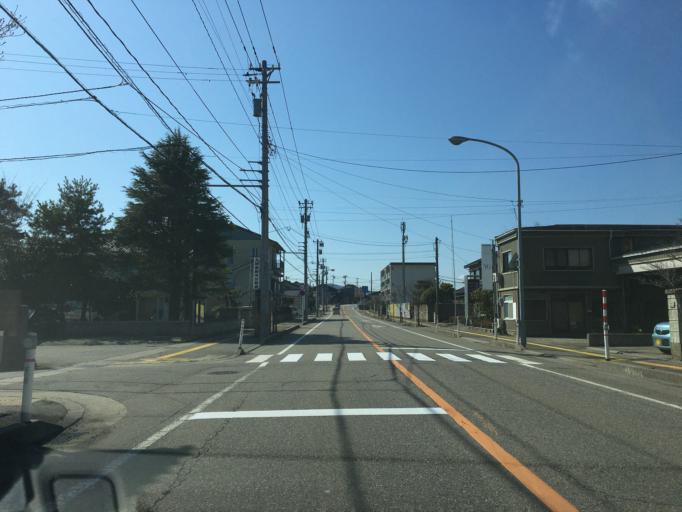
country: JP
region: Toyama
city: Nishishinminato
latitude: 36.7836
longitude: 137.0739
